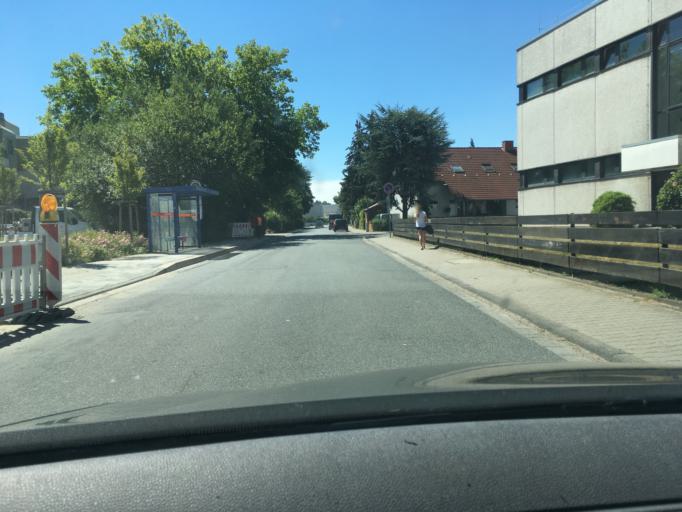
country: DE
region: Hesse
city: Dieburg
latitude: 49.9007
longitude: 8.8546
